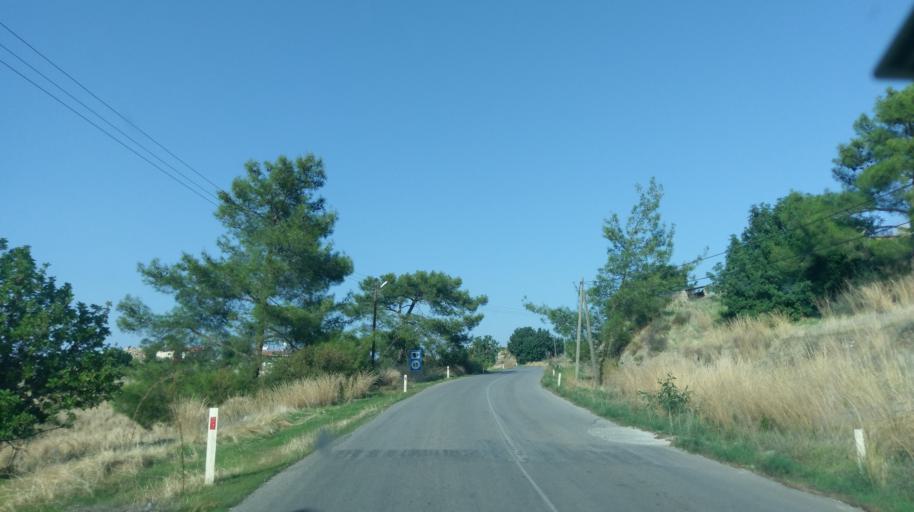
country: CY
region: Lefkosia
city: Kato Pyrgos
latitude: 35.1576
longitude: 32.7612
